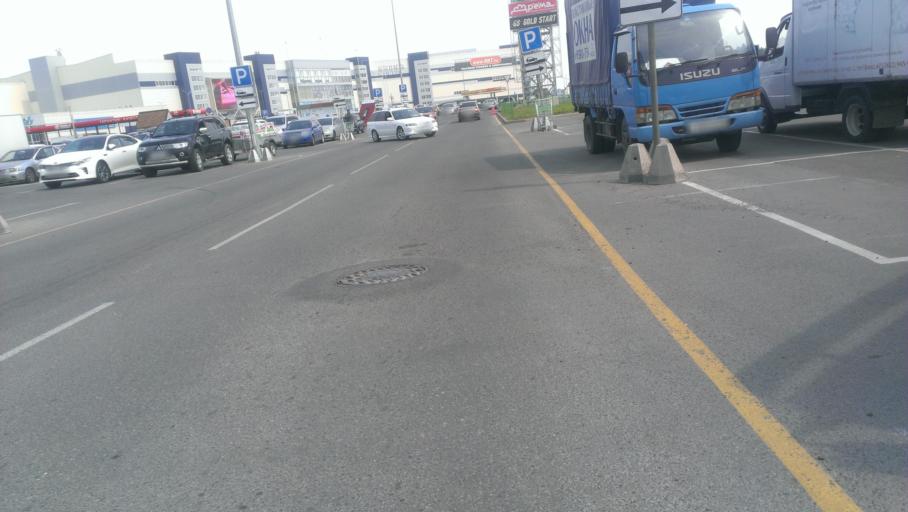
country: RU
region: Altai Krai
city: Novosilikatnyy
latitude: 53.3491
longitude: 83.6320
